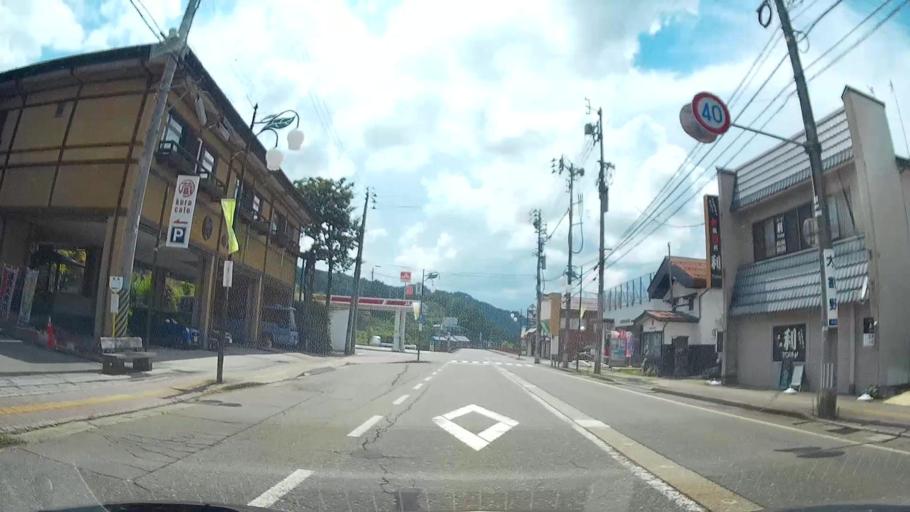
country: JP
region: Niigata
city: Tokamachi
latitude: 37.0127
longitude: 138.6498
